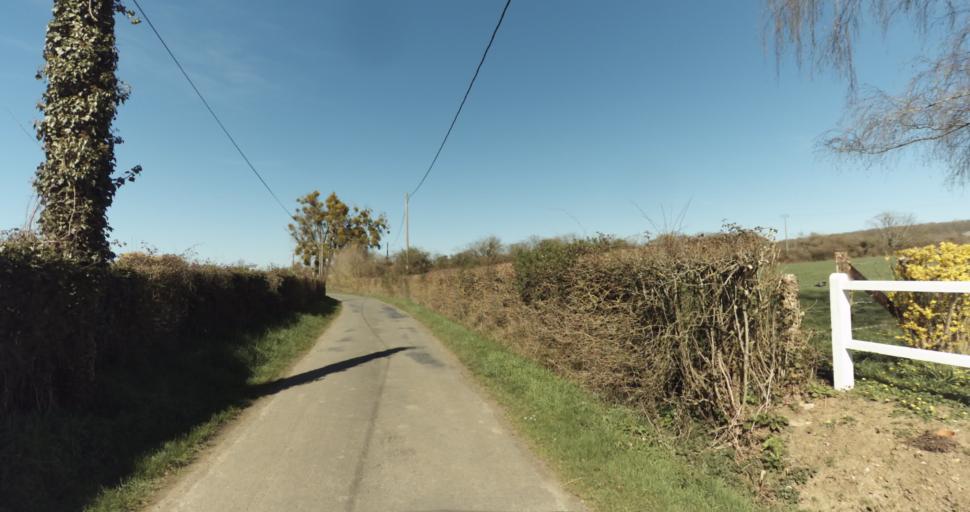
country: FR
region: Lower Normandy
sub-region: Departement du Calvados
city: Saint-Pierre-sur-Dives
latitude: 49.0601
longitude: -0.0263
